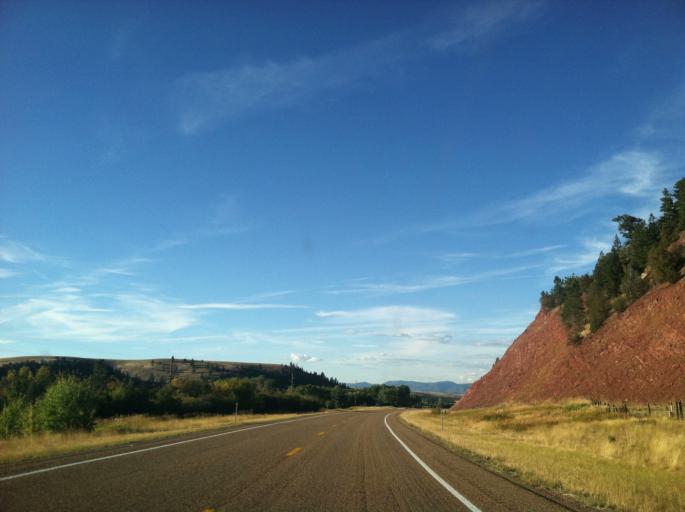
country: US
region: Montana
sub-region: Granite County
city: Philipsburg
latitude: 46.5140
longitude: -113.2274
